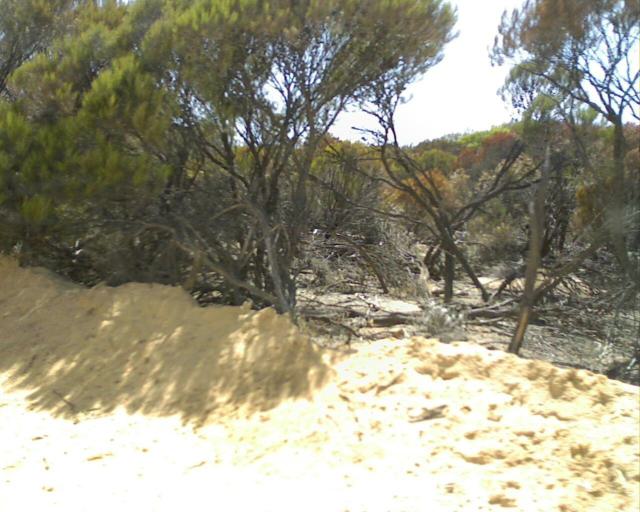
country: AU
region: Western Australia
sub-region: Wongan-Ballidu
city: Wongan Hills
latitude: -30.4281
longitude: 116.9667
